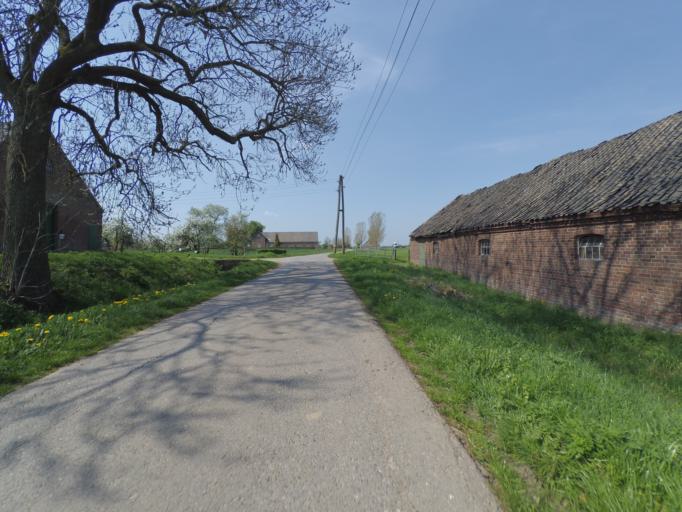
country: NL
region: Gelderland
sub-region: Oude IJsselstreek
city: Gendringen
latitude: 51.8283
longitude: 6.3459
